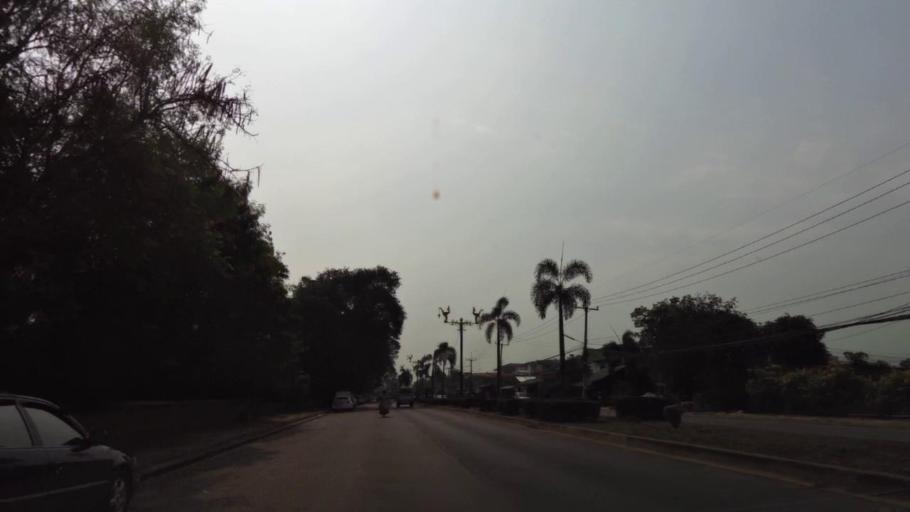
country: TH
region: Phra Nakhon Si Ayutthaya
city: Phra Nakhon Si Ayutthaya
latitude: 14.3478
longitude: 100.5687
